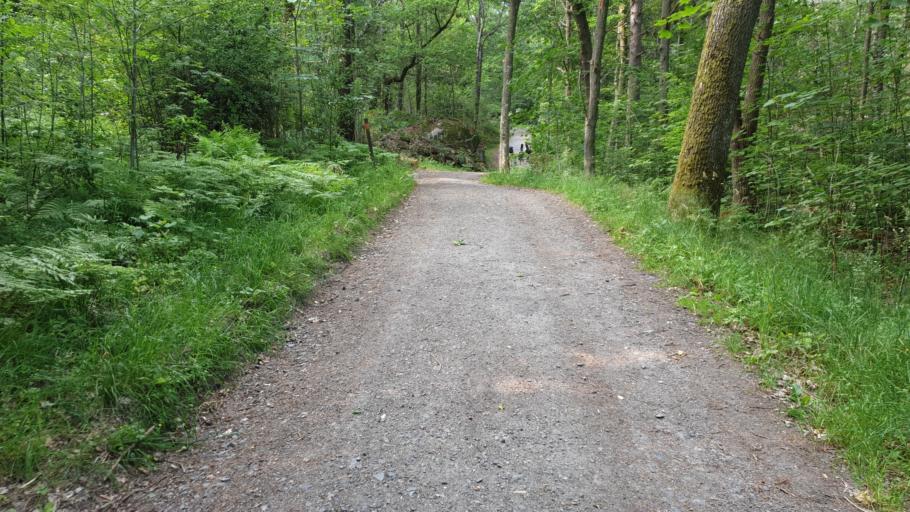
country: SE
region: Vaestra Goetaland
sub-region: Molndal
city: Moelndal
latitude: 57.6665
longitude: 12.0445
